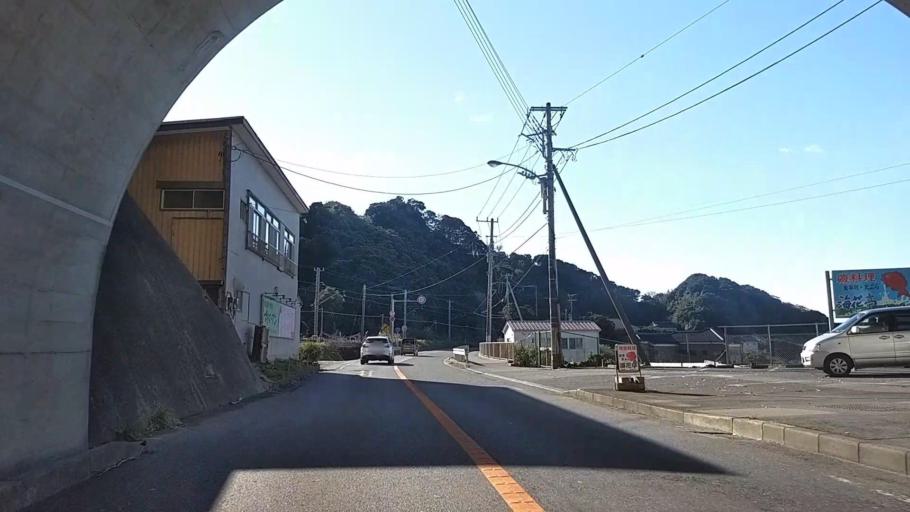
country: JP
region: Chiba
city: Futtsu
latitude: 35.1804
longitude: 139.8194
